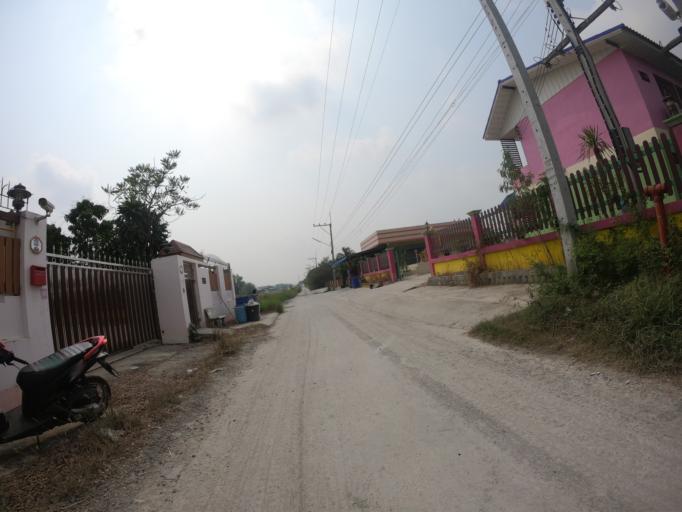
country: TH
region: Pathum Thani
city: Nong Suea
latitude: 14.0666
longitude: 100.8511
